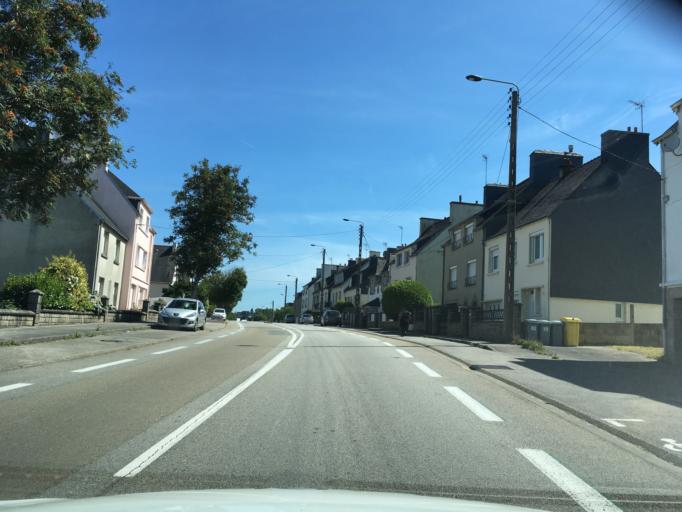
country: FR
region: Brittany
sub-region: Departement du Finistere
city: Quimper
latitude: 47.9770
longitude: -4.1213
